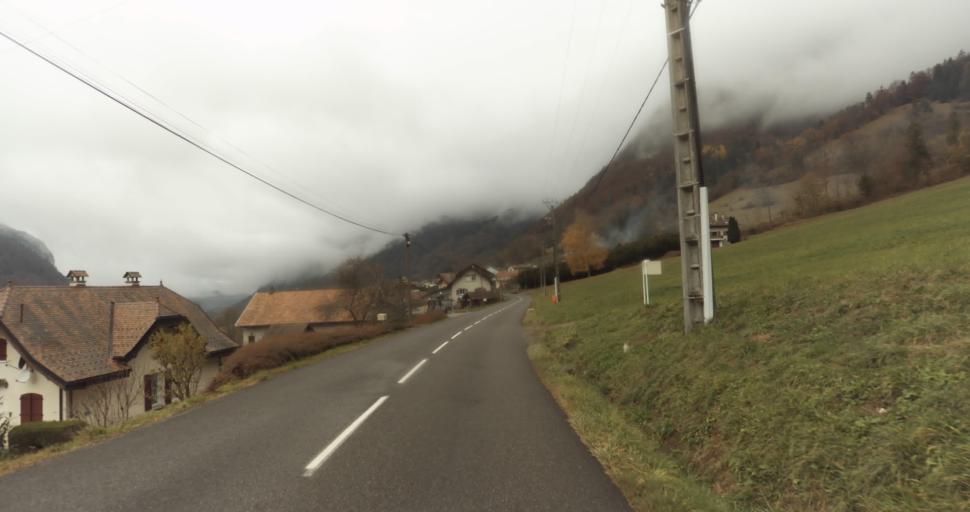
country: FR
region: Rhone-Alpes
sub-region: Departement de la Haute-Savoie
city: Thorens-Glieres
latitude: 45.9754
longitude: 6.2873
